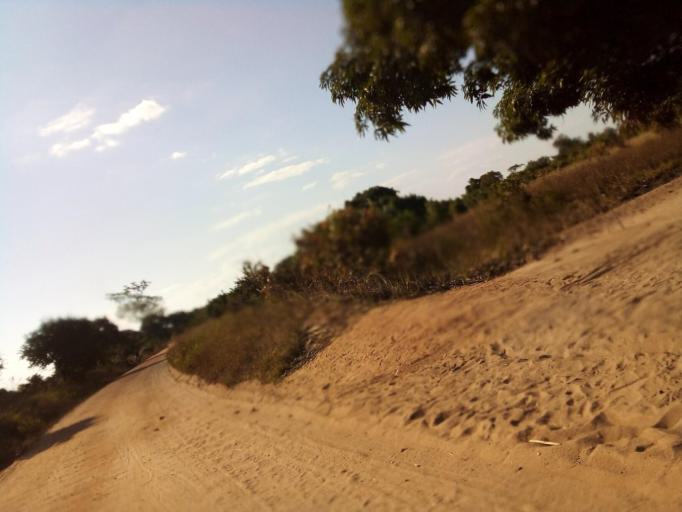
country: MZ
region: Zambezia
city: Quelimane
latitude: -17.5458
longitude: 36.6275
